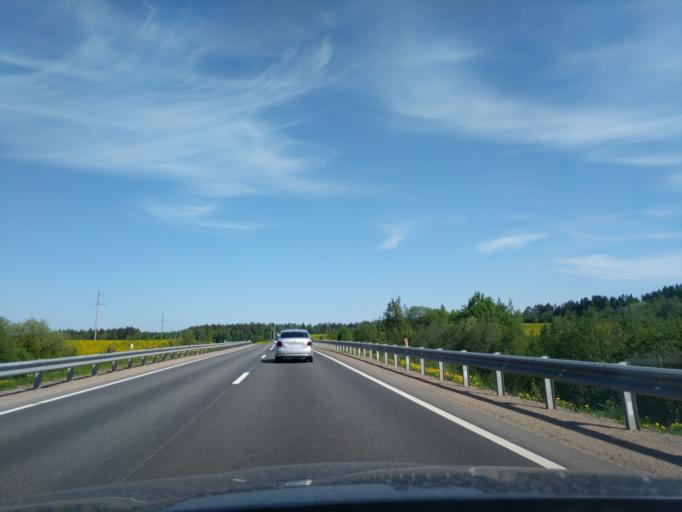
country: BY
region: Minsk
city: Bal'shavik
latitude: 54.0969
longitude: 27.5352
